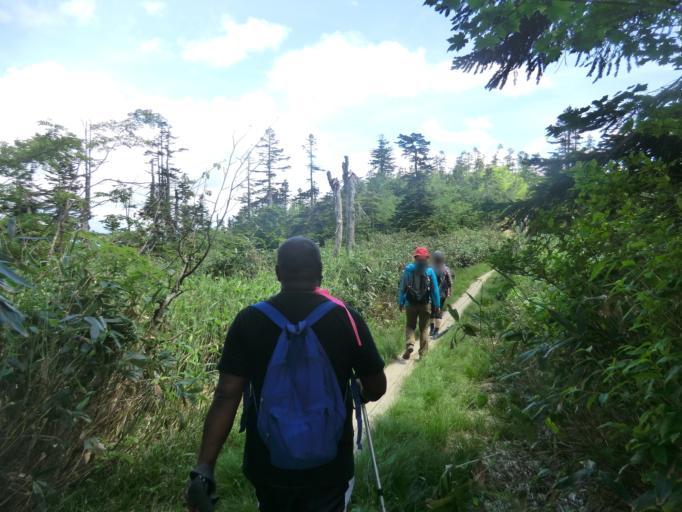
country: JP
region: Gunma
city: Numata
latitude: 36.8867
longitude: 139.1779
